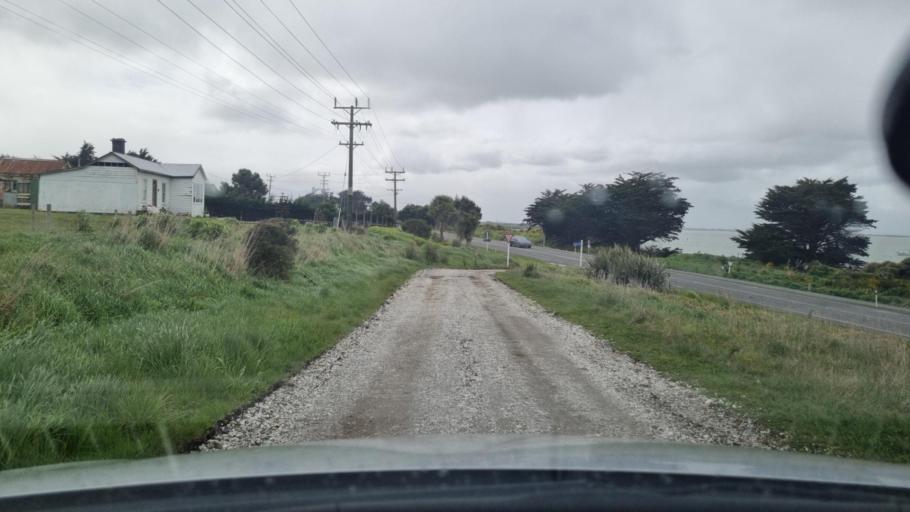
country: NZ
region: Southland
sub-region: Invercargill City
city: Bluff
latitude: -46.5847
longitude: 168.3045
